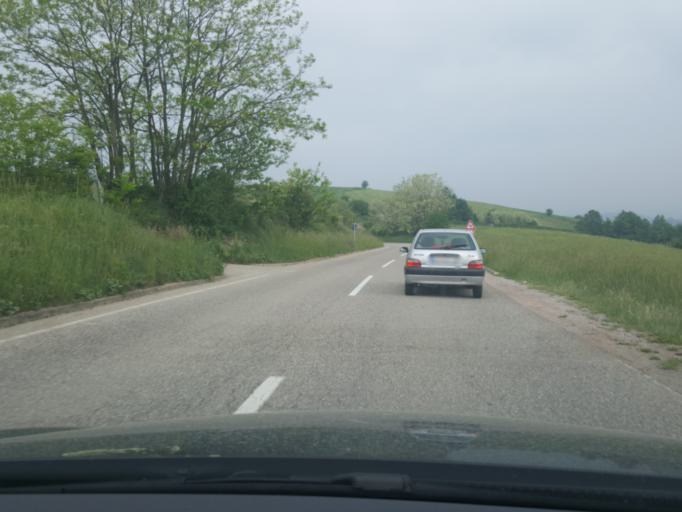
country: RS
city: Kamenica
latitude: 44.2457
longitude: 19.7329
